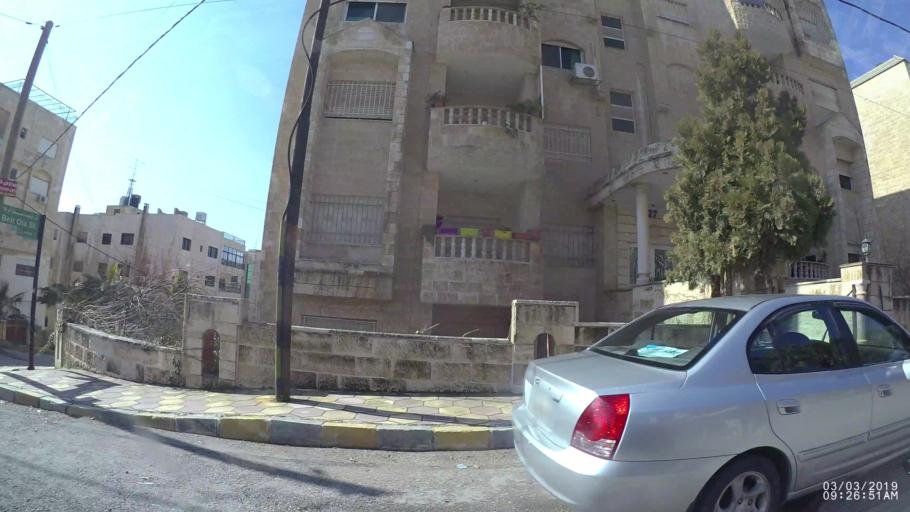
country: JO
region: Amman
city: Al Jubayhah
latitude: 31.9973
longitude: 35.8917
